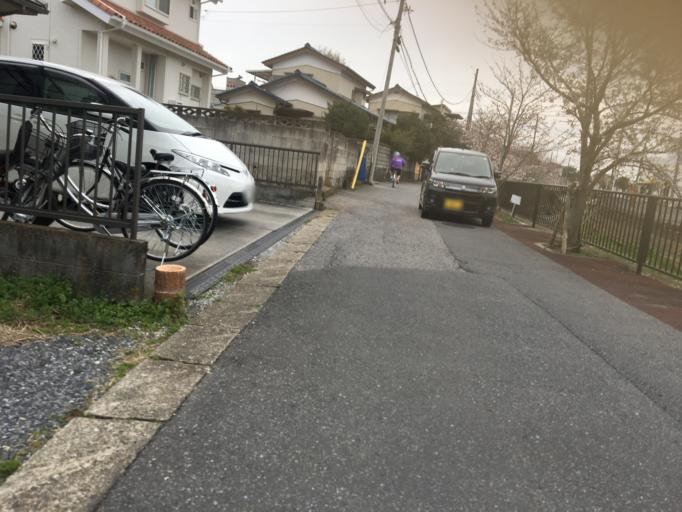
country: JP
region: Saitama
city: Kazo
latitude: 36.1260
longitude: 139.6050
